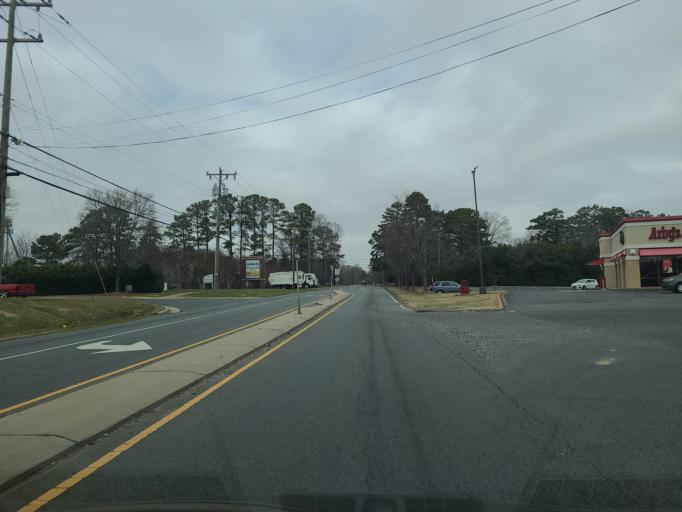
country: US
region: North Carolina
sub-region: Mecklenburg County
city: Mint Hill
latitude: 35.1875
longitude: -80.6888
